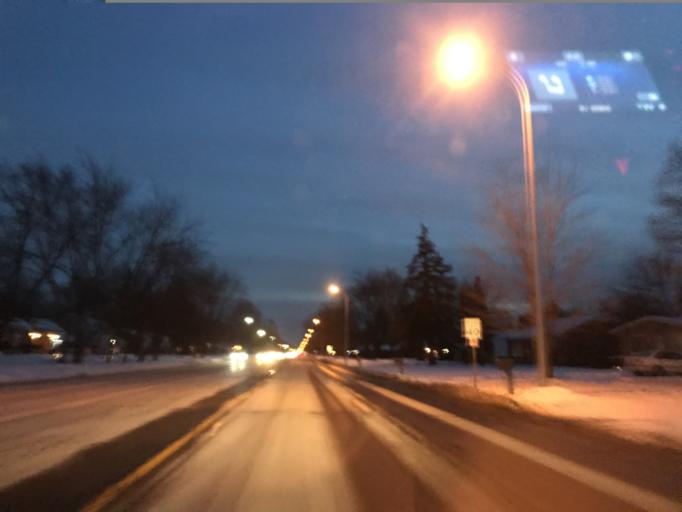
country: US
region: Michigan
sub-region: Wayne County
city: Redford
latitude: 42.3978
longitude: -83.3150
